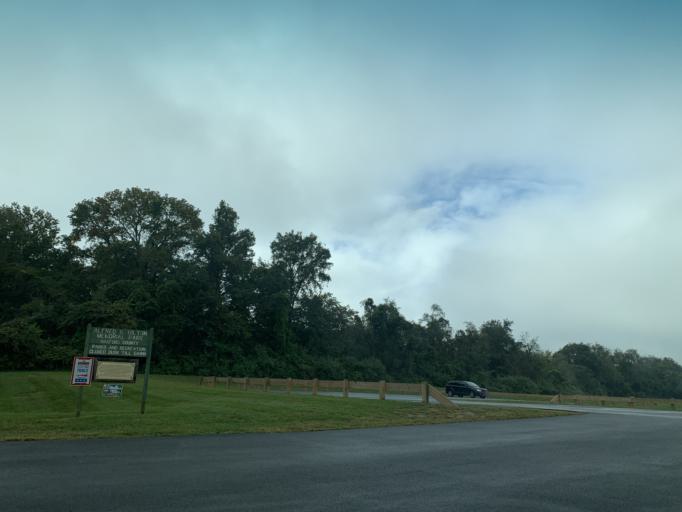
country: US
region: Maryland
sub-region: Harford County
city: Aberdeen
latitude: 39.5662
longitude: -76.1637
